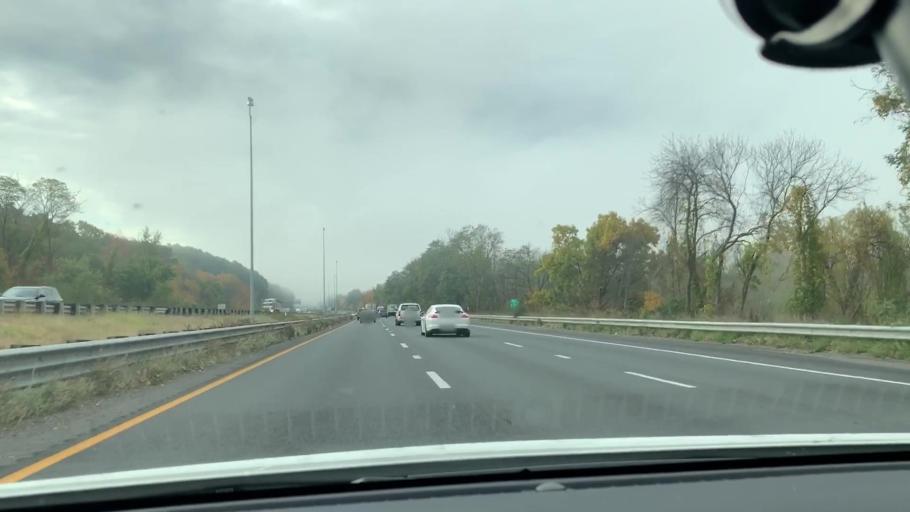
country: US
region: Massachusetts
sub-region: Hampden County
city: Longmeadow
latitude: 42.0571
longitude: -72.5894
